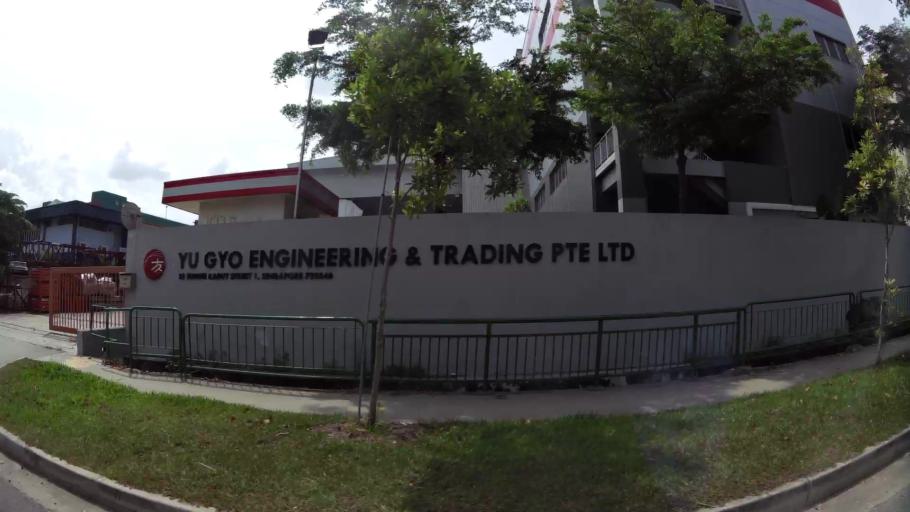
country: MY
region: Johor
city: Johor Bahru
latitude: 1.4143
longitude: 103.7516
